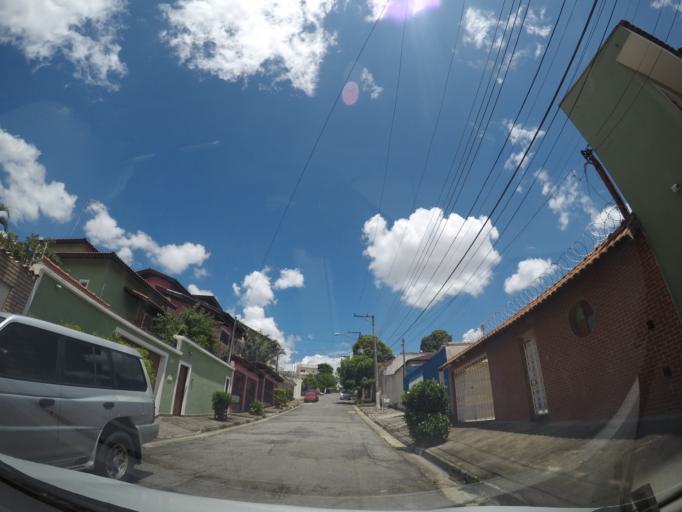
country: BR
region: Sao Paulo
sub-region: Guarulhos
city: Guarulhos
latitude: -23.4518
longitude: -46.5384
